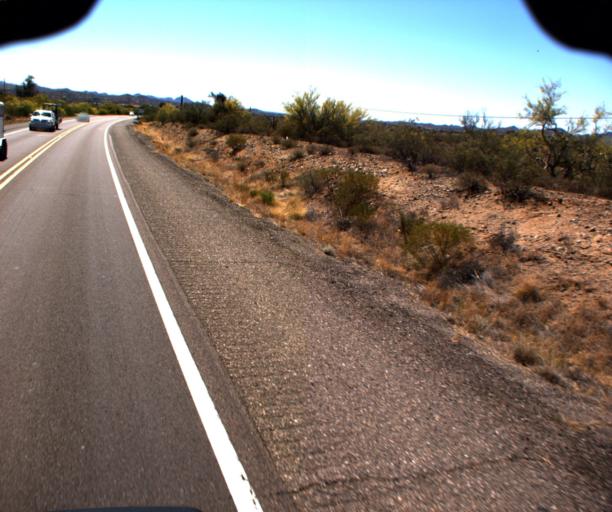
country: US
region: Arizona
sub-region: Maricopa County
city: Wickenburg
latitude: 33.9986
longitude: -112.7600
